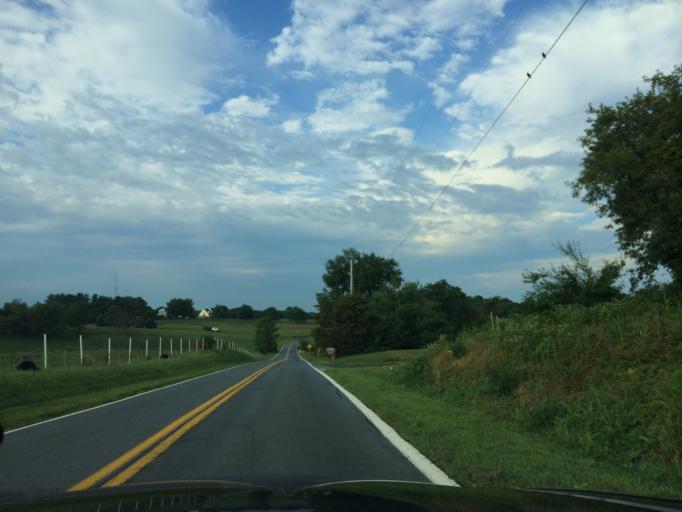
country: US
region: Maryland
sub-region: Montgomery County
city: Damascus
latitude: 39.3273
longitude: -77.2250
